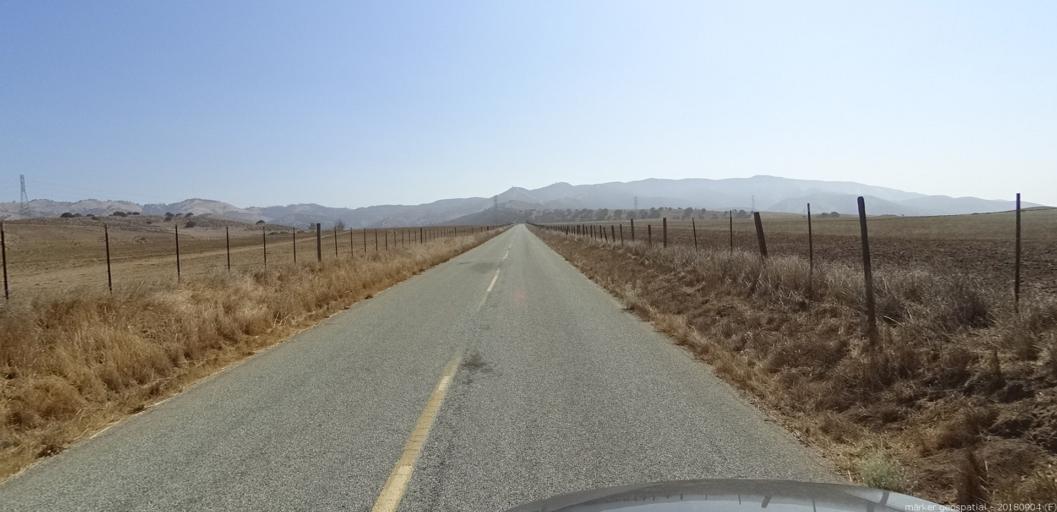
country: US
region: California
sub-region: Monterey County
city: Gonzales
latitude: 36.5113
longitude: -121.3644
